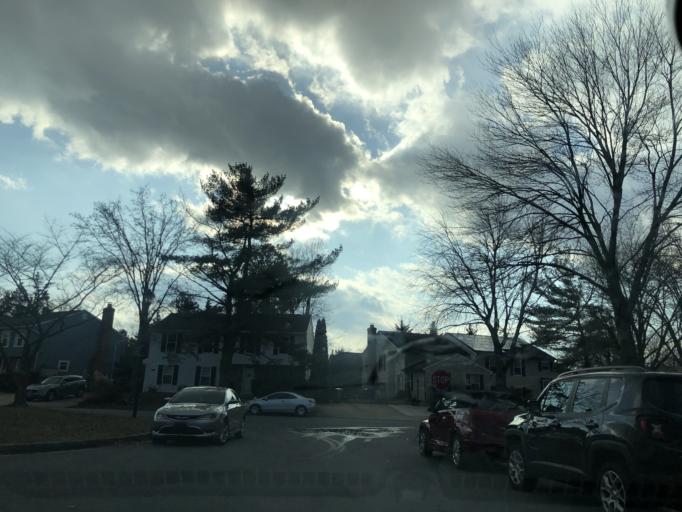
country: US
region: Maryland
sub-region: Howard County
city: Columbia
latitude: 39.2006
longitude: -76.8354
